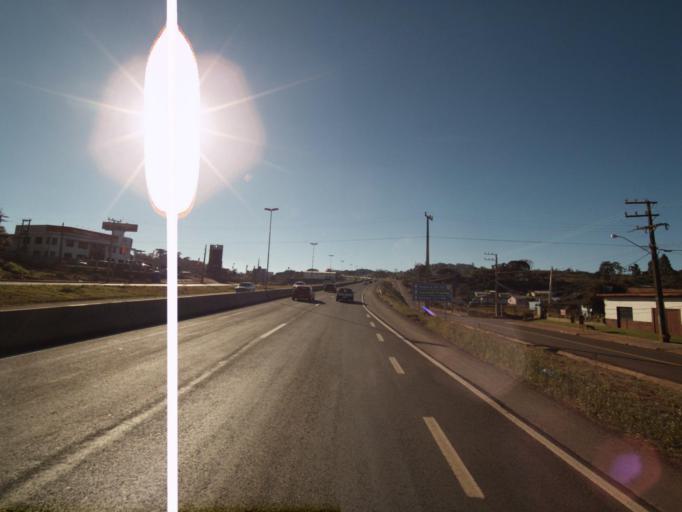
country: BR
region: Santa Catarina
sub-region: Chapeco
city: Chapeco
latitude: -27.0071
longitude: -52.6425
